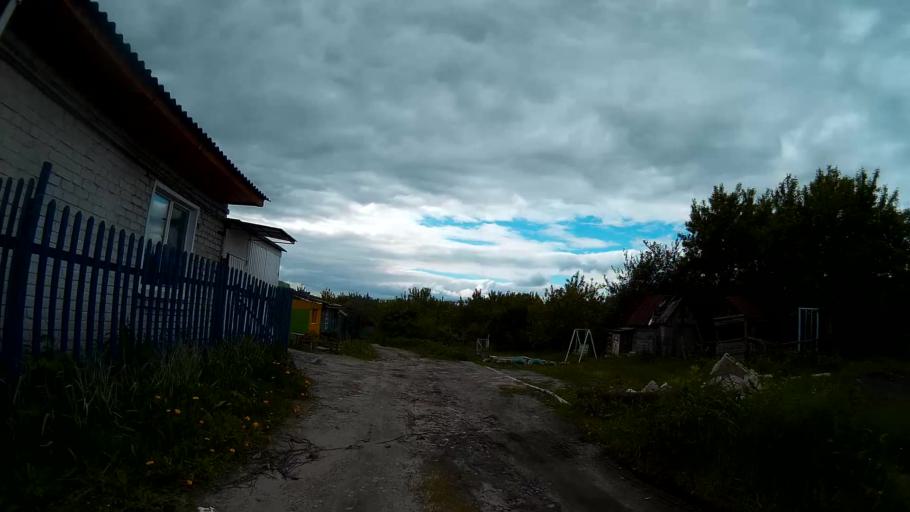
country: RU
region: Ulyanovsk
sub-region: Ulyanovskiy Rayon
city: Ulyanovsk
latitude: 54.2603
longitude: 48.3071
